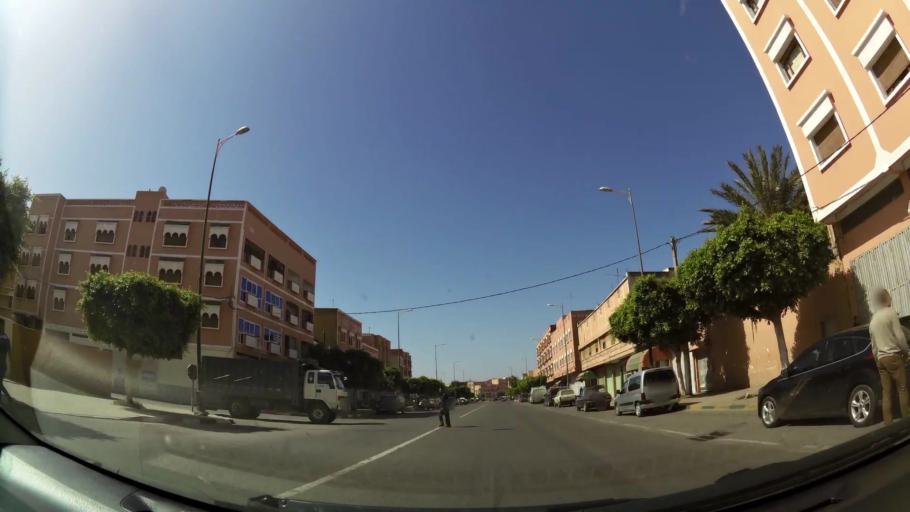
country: MA
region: Souss-Massa-Draa
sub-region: Inezgane-Ait Mellou
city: Inezgane
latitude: 30.3401
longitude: -9.5028
